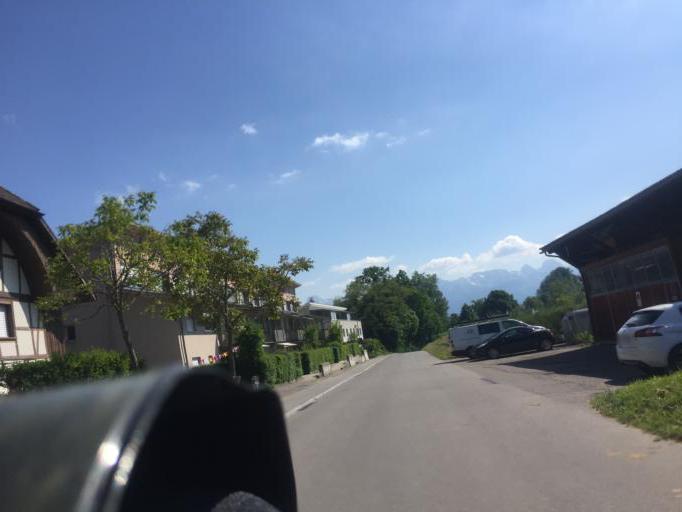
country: CH
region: Bern
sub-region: Bern-Mittelland District
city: Munsingen
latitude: 46.8448
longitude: 7.5450
